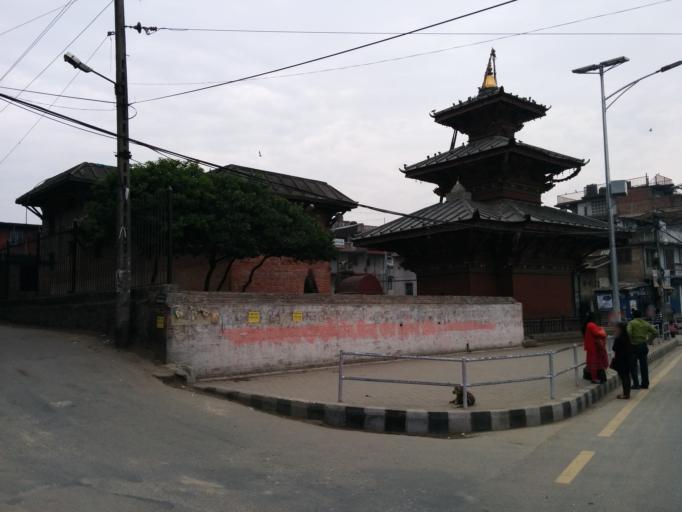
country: NP
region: Central Region
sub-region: Bagmati Zone
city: Kathmandu
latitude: 27.7100
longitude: 85.3440
